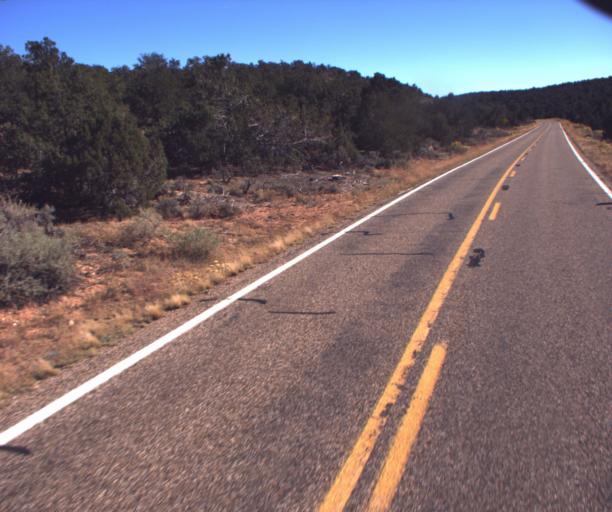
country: US
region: Arizona
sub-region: Coconino County
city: Fredonia
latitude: 36.7362
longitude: -112.0985
